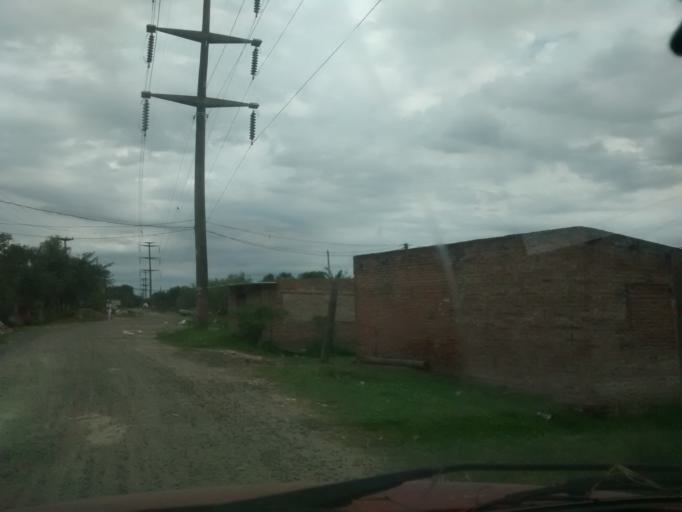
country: AR
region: Chaco
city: Resistencia
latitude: -27.4232
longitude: -58.9750
